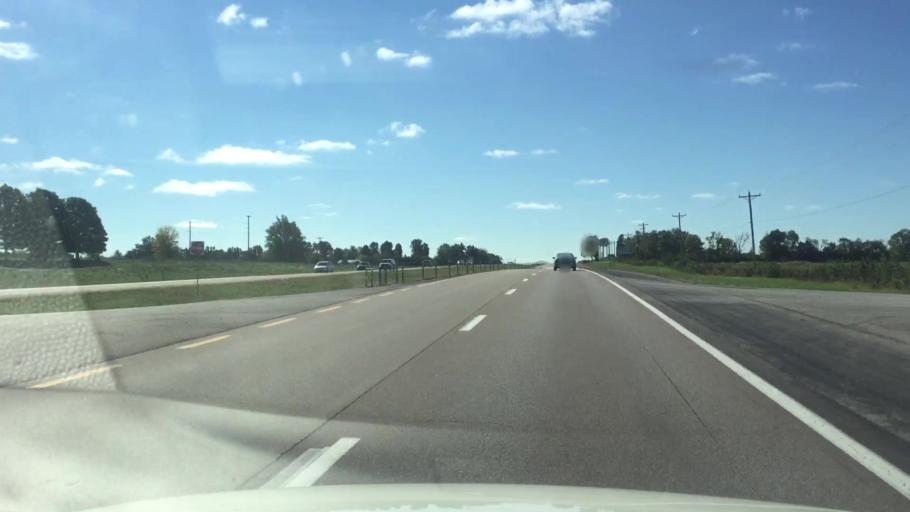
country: US
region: Missouri
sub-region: Boone County
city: Ashland
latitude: 38.7891
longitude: -92.2523
